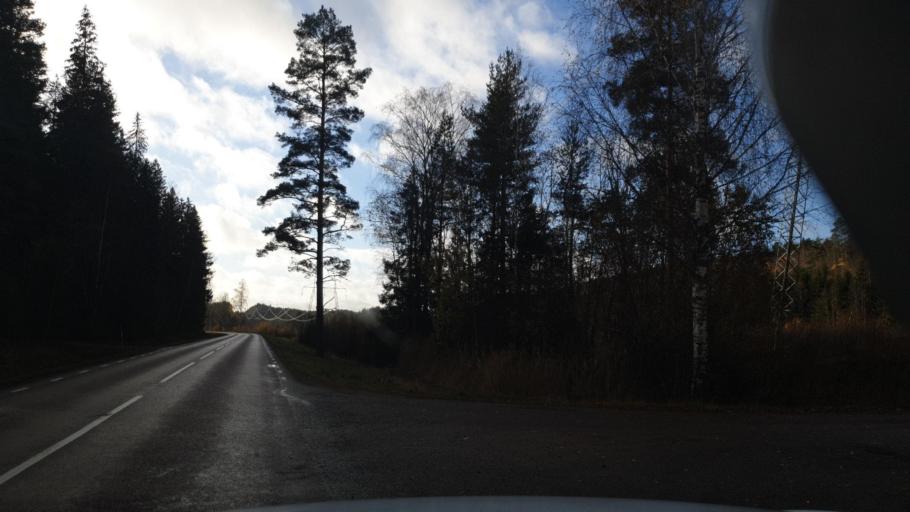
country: SE
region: Vaermland
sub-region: Grums Kommun
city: Grums
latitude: 59.4306
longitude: 12.9770
